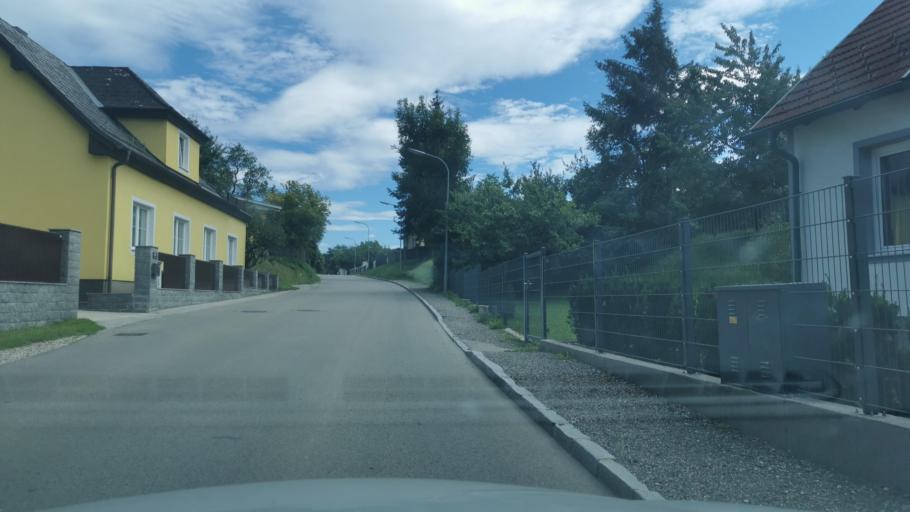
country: AT
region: Lower Austria
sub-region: Politischer Bezirk Sankt Polten
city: Pyhra
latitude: 48.1525
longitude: 15.6402
